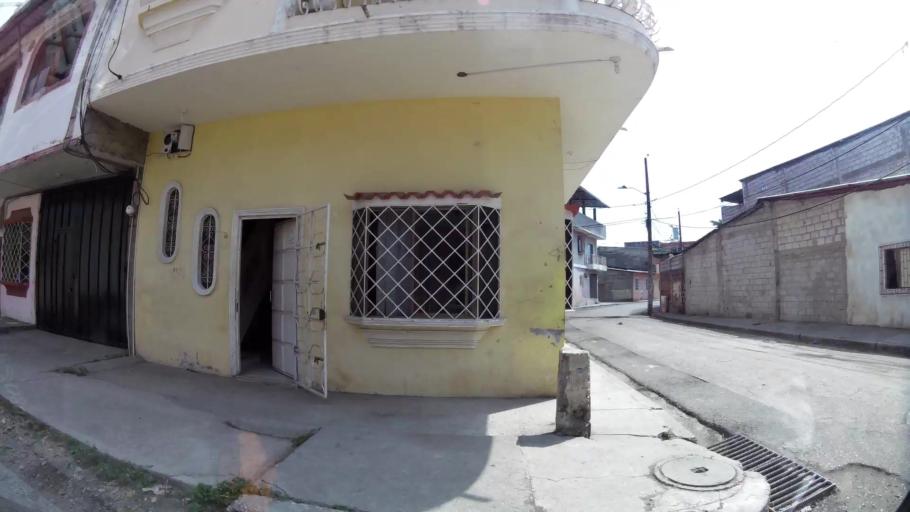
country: EC
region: Guayas
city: Guayaquil
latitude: -2.2632
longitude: -79.8866
